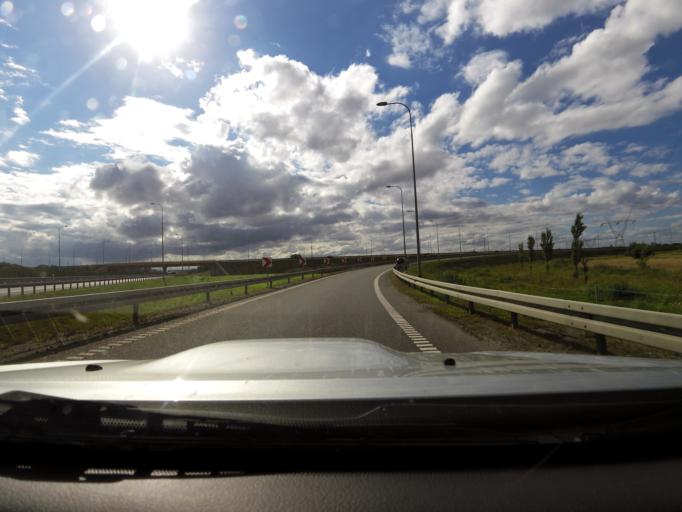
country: PL
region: Pomeranian Voivodeship
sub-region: Gdansk
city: Gdansk
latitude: 54.3204
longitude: 18.7085
